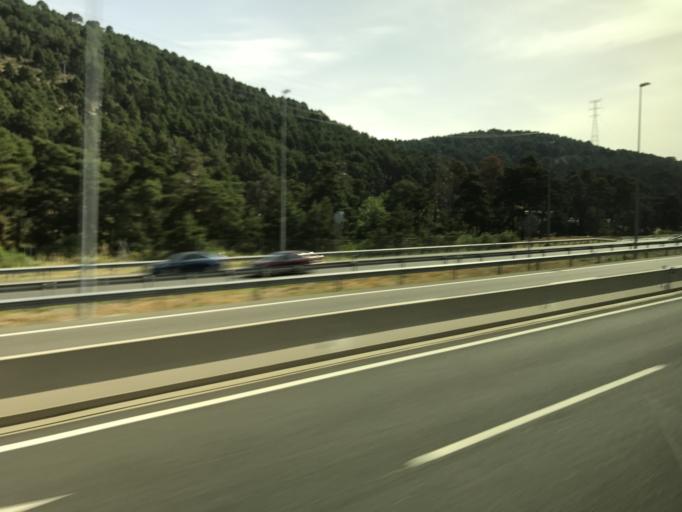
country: ES
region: Madrid
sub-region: Provincia de Madrid
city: Guadarrama
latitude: 40.7138
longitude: -4.1815
